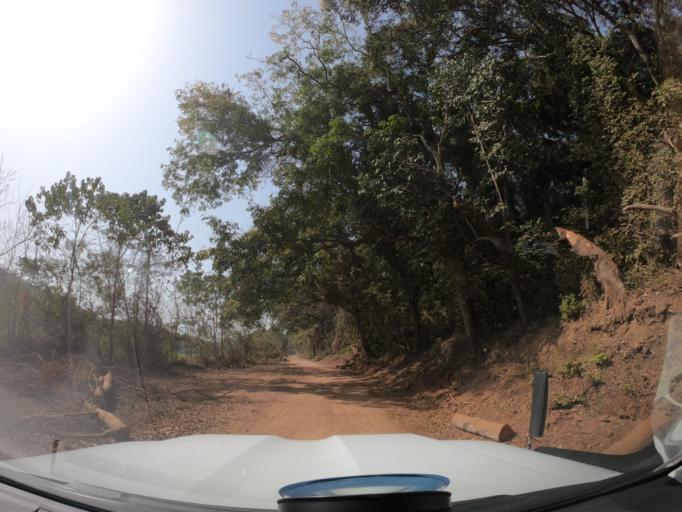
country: GN
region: Mamou
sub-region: Mamou Prefecture
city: Mamou
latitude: 10.5005
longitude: -12.1423
